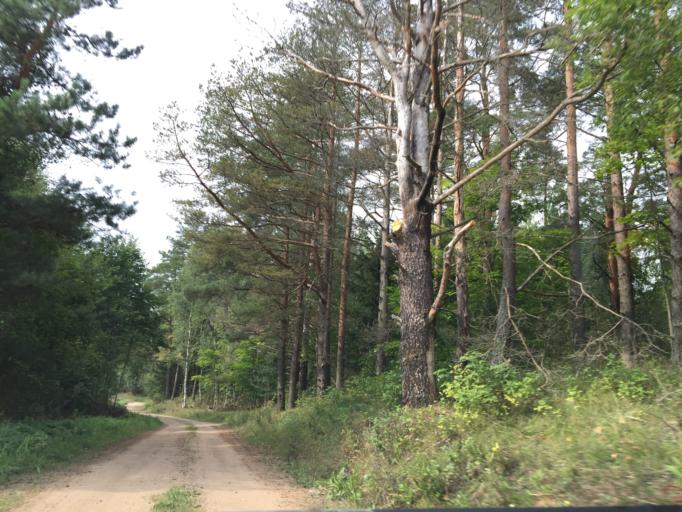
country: LV
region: Cibla
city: Cibla
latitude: 56.2462
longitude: 27.8132
